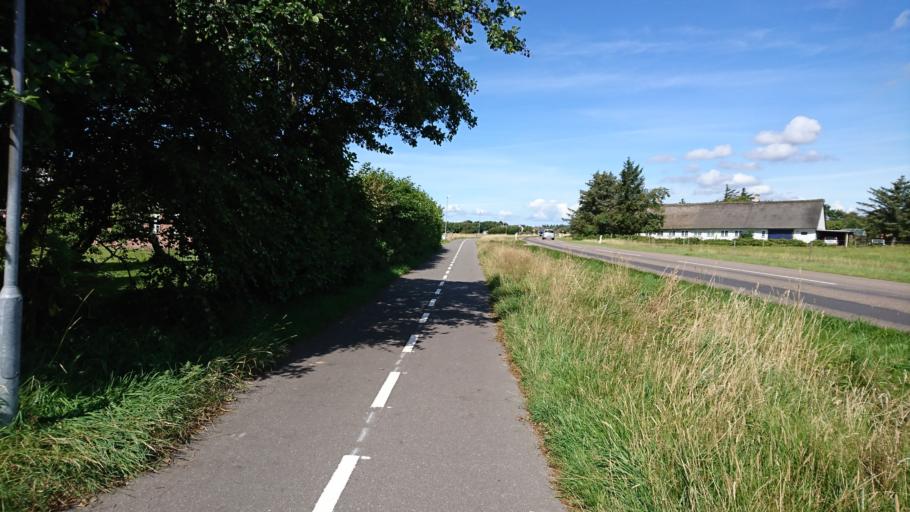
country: DK
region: South Denmark
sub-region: Fano Kommune
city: Nordby
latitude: 55.4277
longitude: 8.3962
